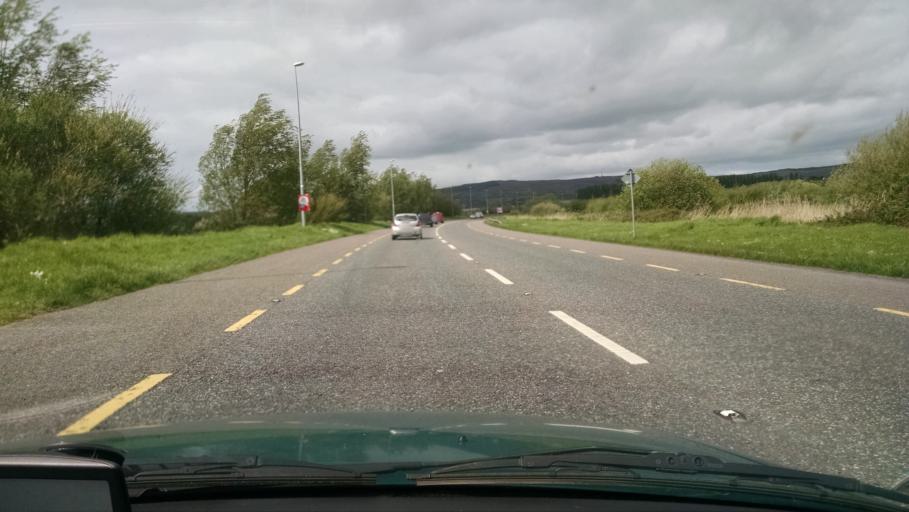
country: IE
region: Munster
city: Moyross
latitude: 52.6676
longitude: -8.6731
